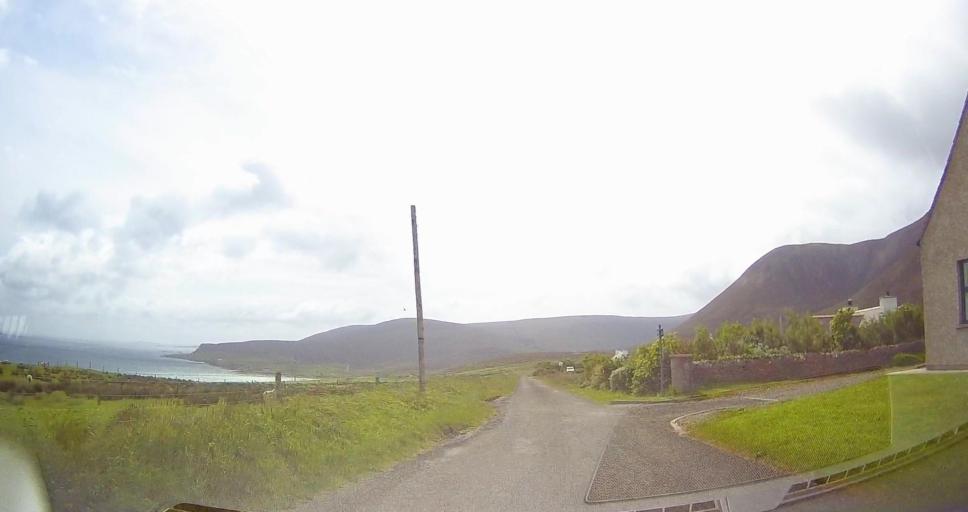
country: GB
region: Scotland
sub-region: Orkney Islands
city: Stromness
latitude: 58.9132
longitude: -3.3318
